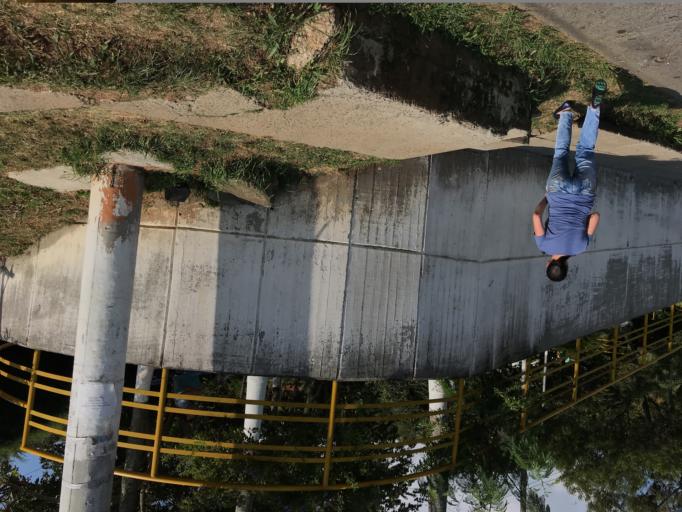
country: CO
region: Valle del Cauca
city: Cali
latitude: 3.4821
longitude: -76.6070
